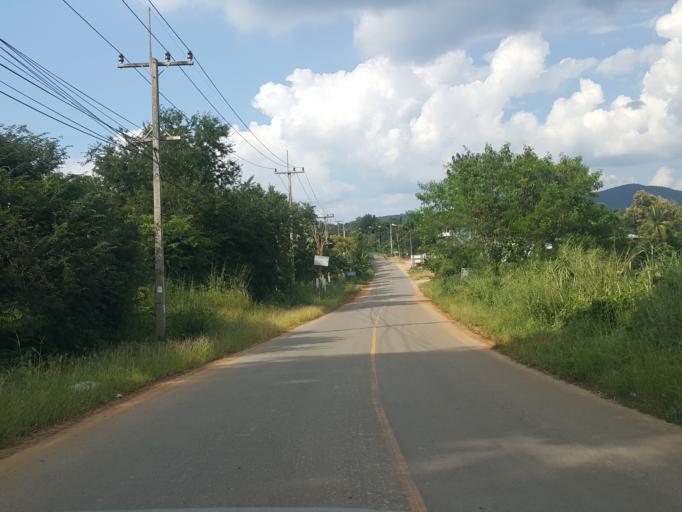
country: TH
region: Chiang Mai
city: Mae Chaem
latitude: 18.5178
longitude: 98.3627
